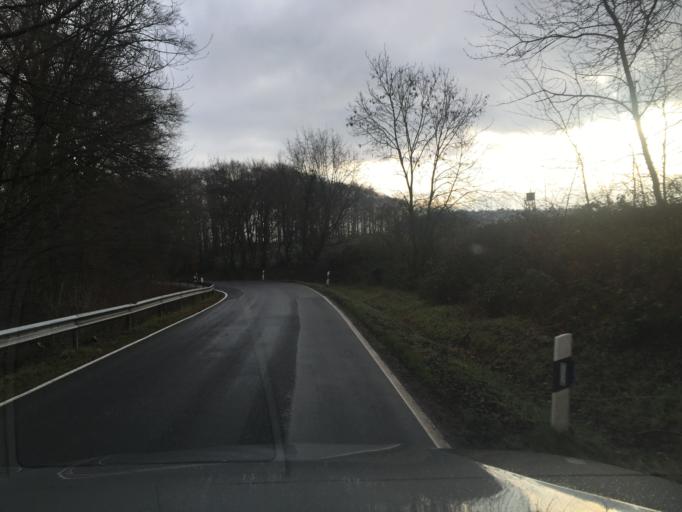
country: DE
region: Rheinland-Pfalz
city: Unkel
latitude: 50.5780
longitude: 7.1830
